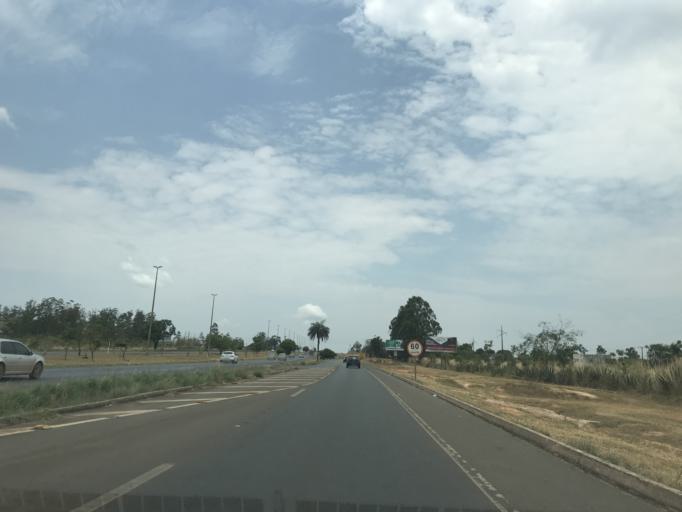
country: BR
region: Federal District
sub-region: Brasilia
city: Brasilia
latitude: -15.6681
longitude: -47.8131
